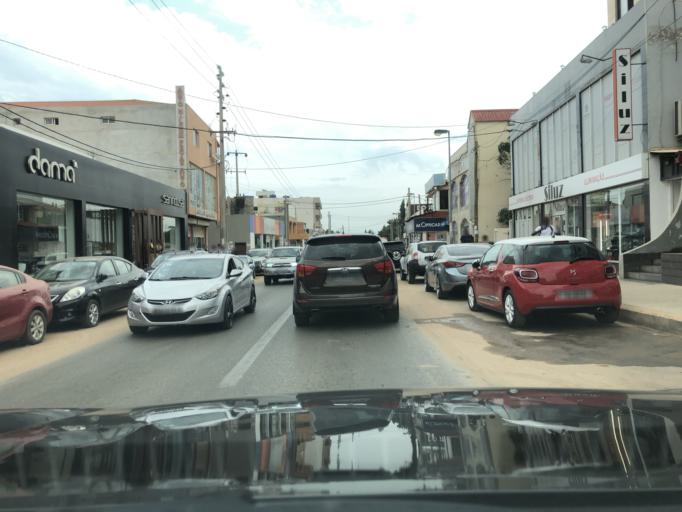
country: AO
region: Luanda
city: Luanda
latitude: -8.8937
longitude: 13.1995
